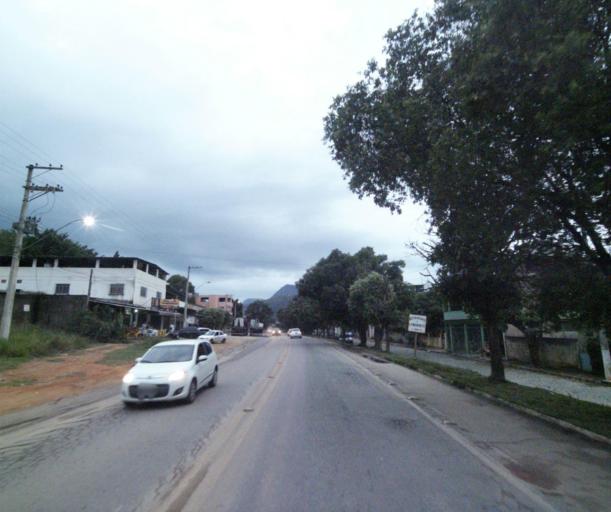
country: BR
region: Espirito Santo
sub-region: Castelo
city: Castelo
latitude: -20.6333
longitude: -41.2057
